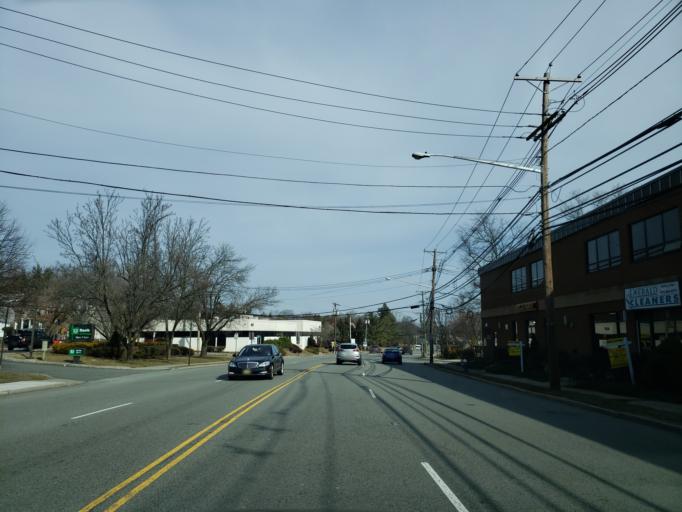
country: US
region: New Jersey
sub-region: Essex County
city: West Orange
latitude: 40.8113
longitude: -74.2601
